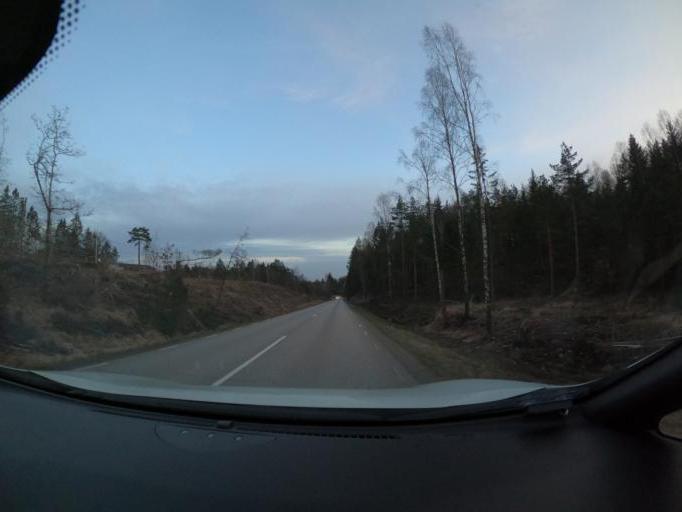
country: SE
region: Vaestra Goetaland
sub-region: Harryda Kommun
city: Molnlycke
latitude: 57.6467
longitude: 12.1595
